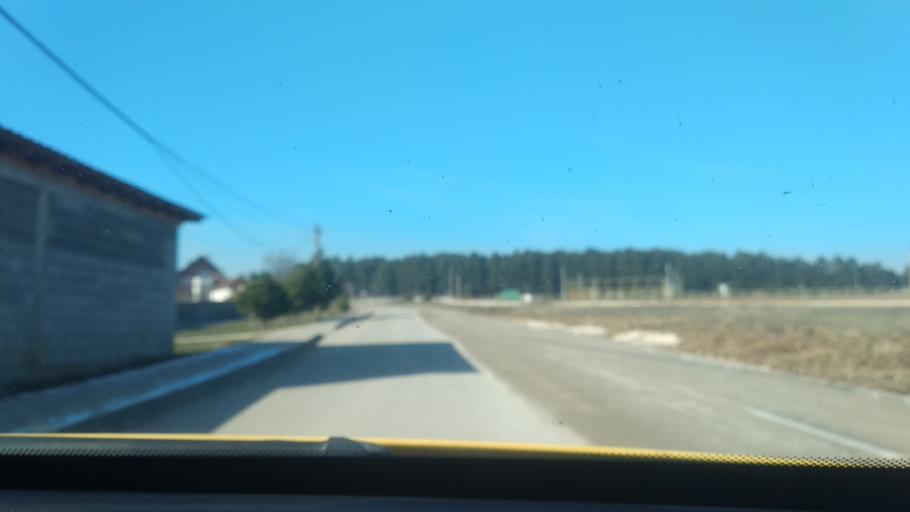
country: XK
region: Pristina
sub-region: Komuna e Gracanices
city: Glanica
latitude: 42.6087
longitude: 21.0238
